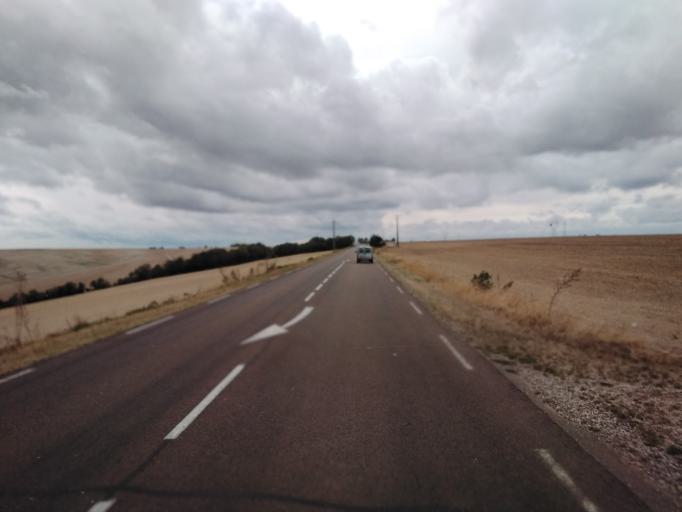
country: FR
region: Champagne-Ardenne
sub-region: Departement de la Marne
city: Frignicourt
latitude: 48.6138
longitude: 4.5648
